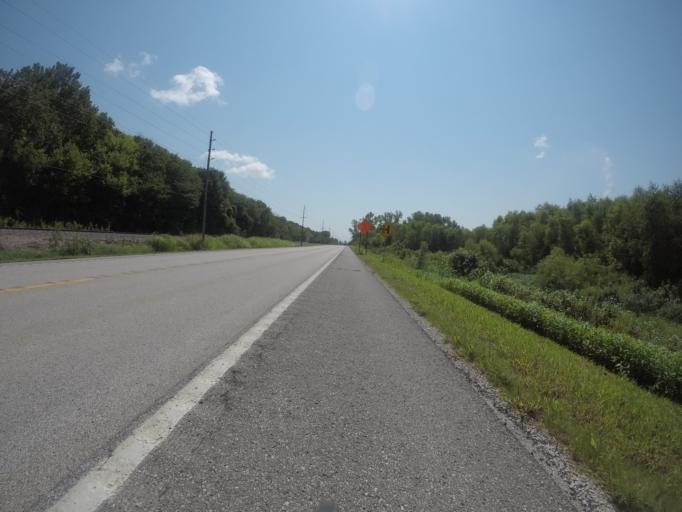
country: US
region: Missouri
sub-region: Platte County
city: Weston
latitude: 39.4666
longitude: -94.9767
